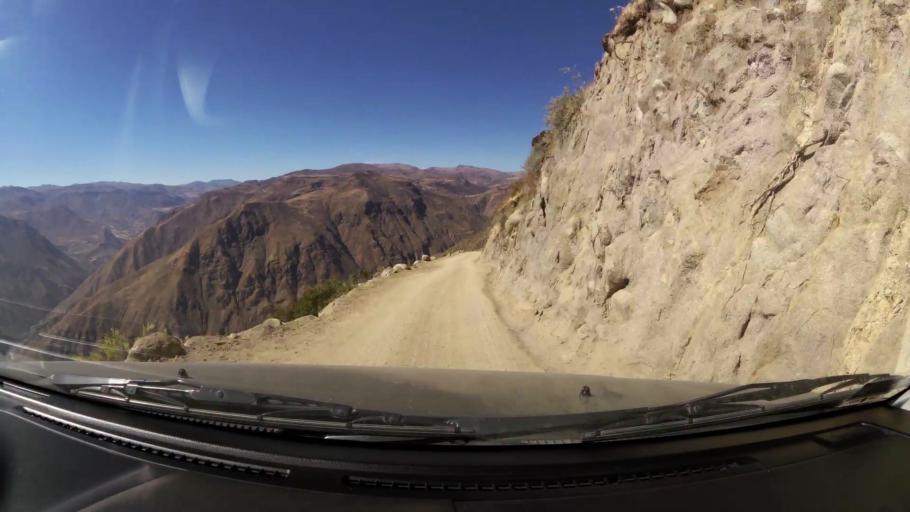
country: PE
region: Huancavelica
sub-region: Huaytara
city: Quito-Arma
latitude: -13.6172
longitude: -75.3532
